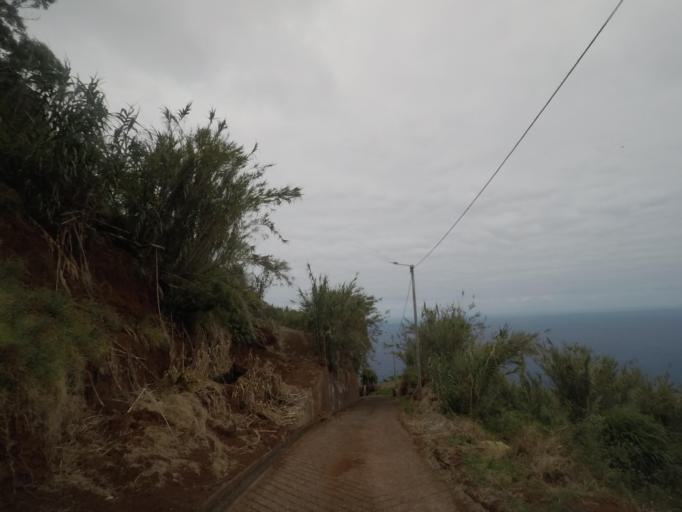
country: PT
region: Madeira
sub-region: Porto Moniz
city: Porto Moniz
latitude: 32.8626
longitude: -17.1805
